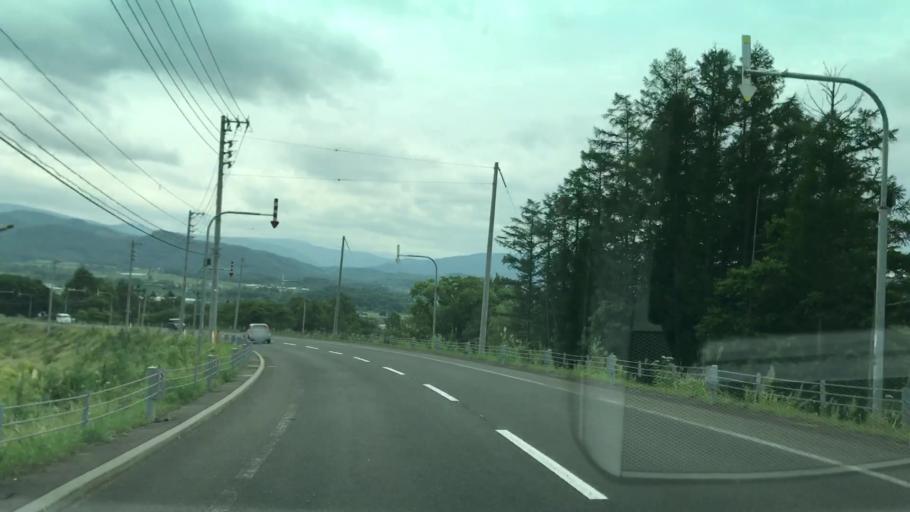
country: JP
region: Hokkaido
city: Yoichi
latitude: 43.1101
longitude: 140.8193
